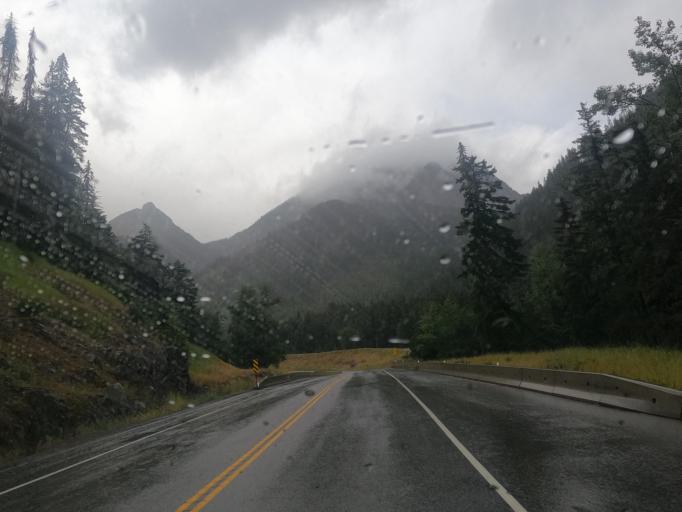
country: CA
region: British Columbia
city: Lillooet
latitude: 50.5337
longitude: -122.1491
